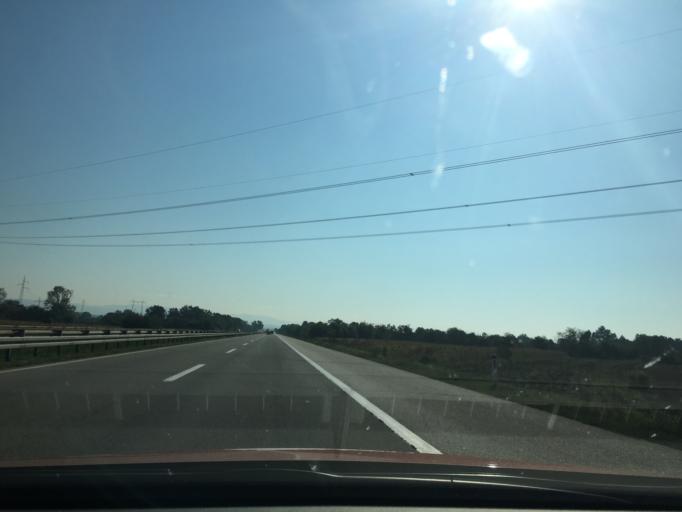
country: RS
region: Central Serbia
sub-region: Pomoravski Okrug
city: Cuprija
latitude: 43.9624
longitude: 21.3312
